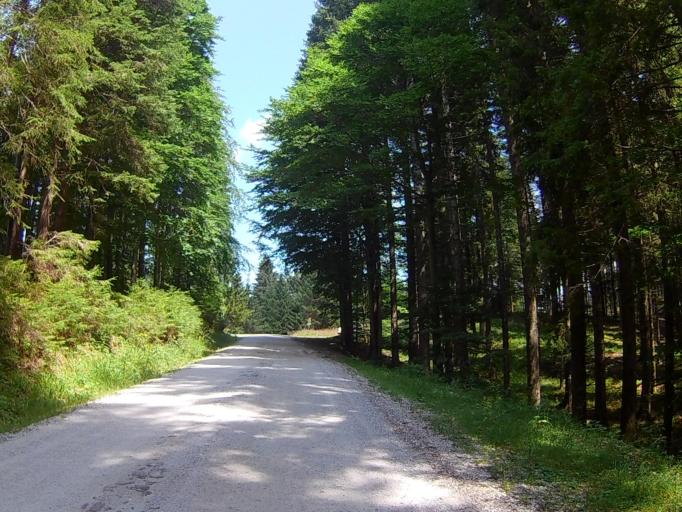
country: SI
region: Lovrenc na Pohorju
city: Lovrenc na Pohorju
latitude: 46.4824
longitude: 15.4451
